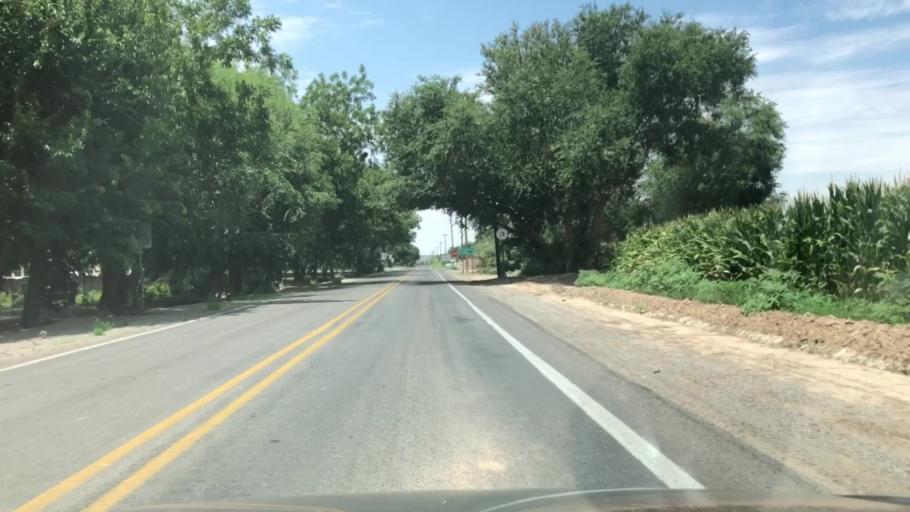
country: US
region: New Mexico
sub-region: Dona Ana County
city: Vado
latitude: 32.1117
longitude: -106.6821
